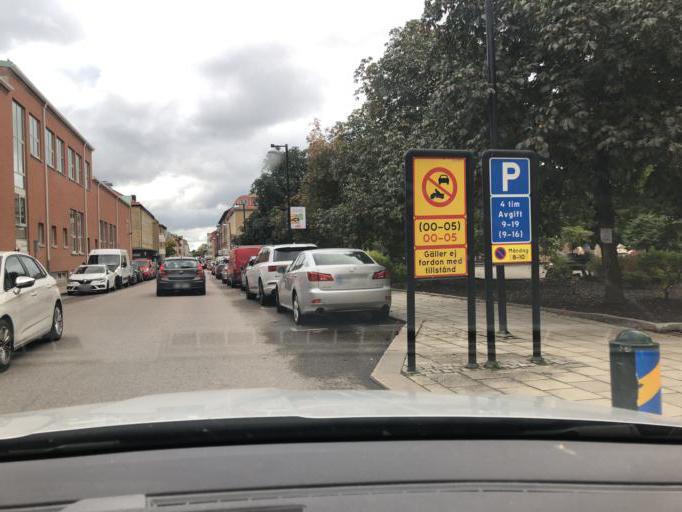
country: SE
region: Vaestra Goetaland
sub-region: Trollhattan
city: Trollhattan
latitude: 58.2869
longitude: 12.2912
